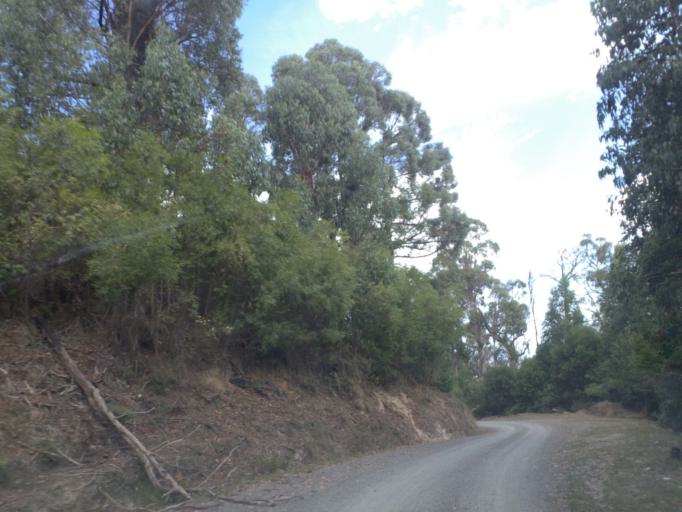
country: AU
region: Victoria
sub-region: Murrindindi
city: Alexandra
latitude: -37.4140
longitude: 145.7586
